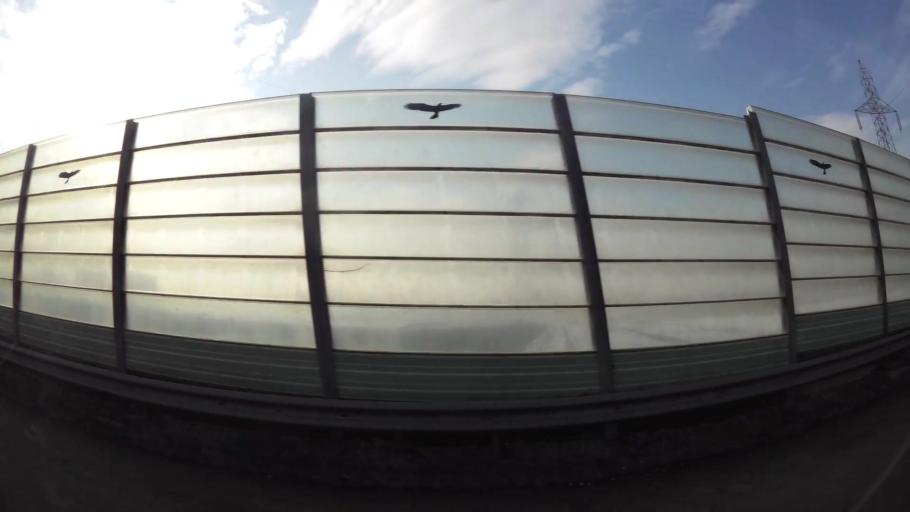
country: MK
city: Creshevo
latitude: 42.0284
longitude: 21.5296
